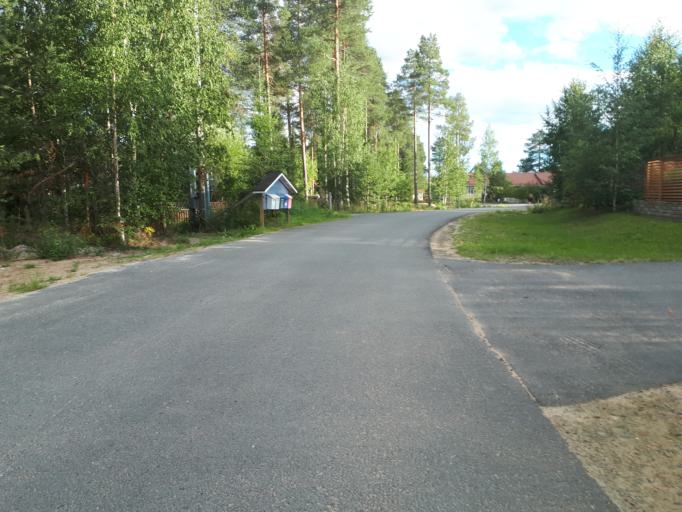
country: FI
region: Northern Ostrobothnia
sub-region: Oulunkaari
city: Ii
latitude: 65.3258
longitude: 25.4185
